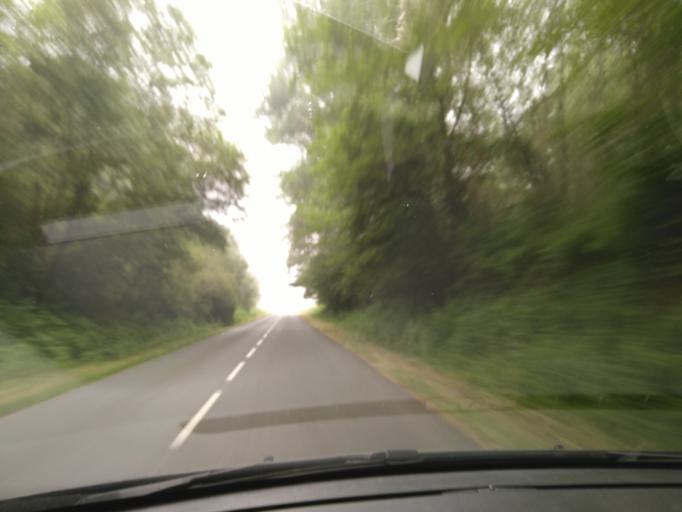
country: FR
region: Aquitaine
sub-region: Departement des Landes
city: Villeneuve-de-Marsan
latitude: 43.8688
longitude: -0.2412
